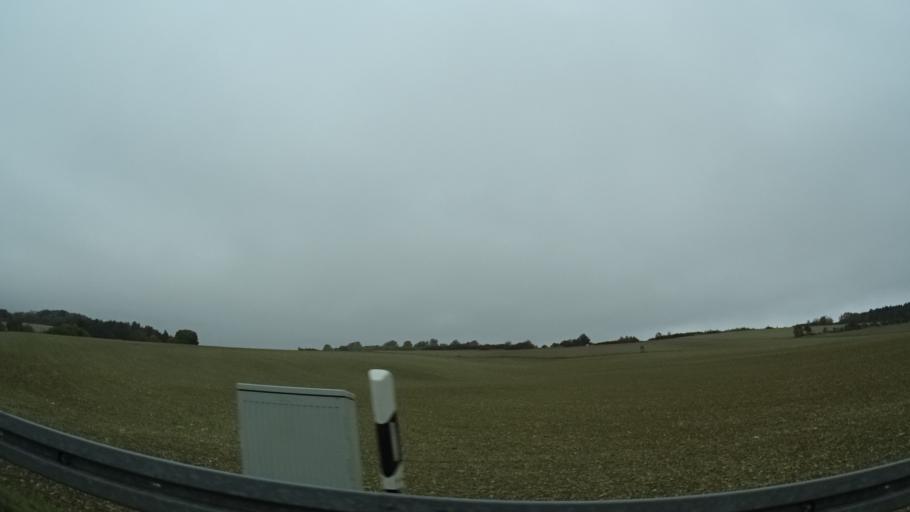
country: DE
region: Thuringia
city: Erbenhausen
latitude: 50.5937
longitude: 10.1495
